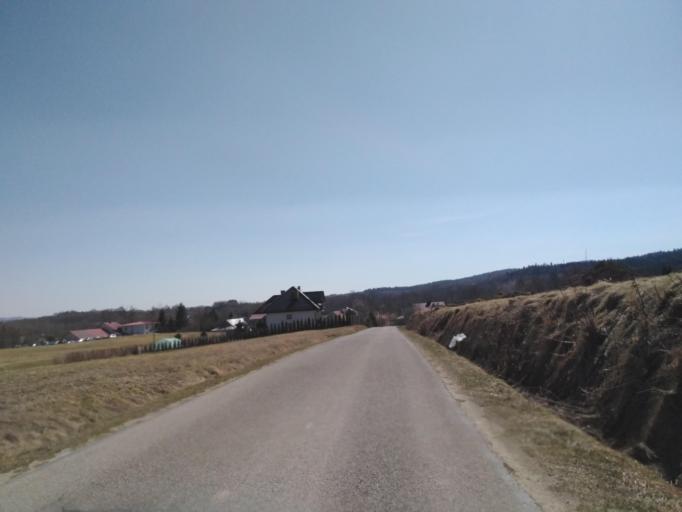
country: PL
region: Subcarpathian Voivodeship
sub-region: Powiat brzozowski
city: Orzechowka
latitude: 49.7170
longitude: 21.9638
